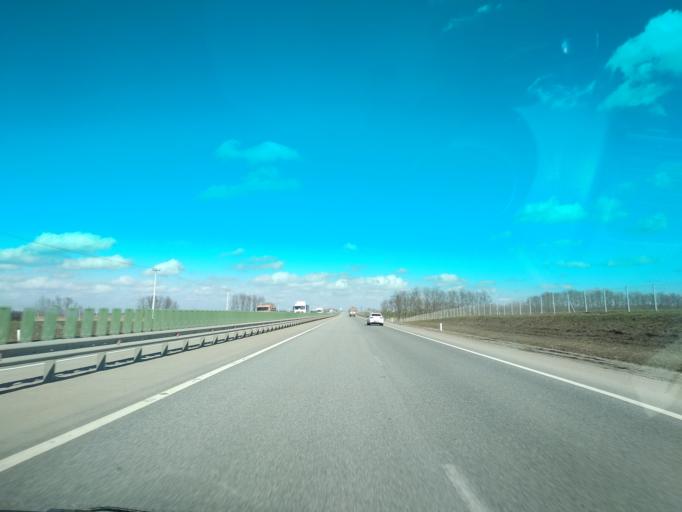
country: RU
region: Krasnodarskiy
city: Platnirovskaya
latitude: 45.4473
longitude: 39.3730
